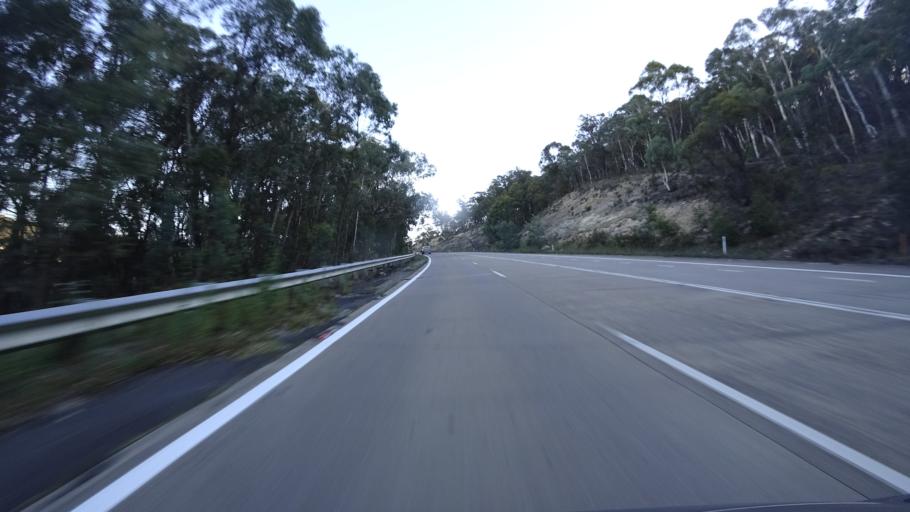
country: AU
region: New South Wales
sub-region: Lithgow
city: Portland
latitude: -33.3329
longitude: 150.0364
